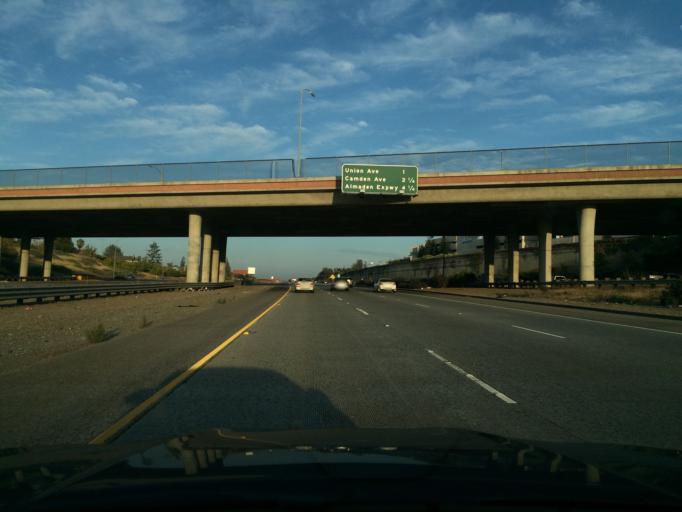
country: US
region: California
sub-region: Santa Clara County
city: Cambrian Park
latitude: 37.2546
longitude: -121.9524
